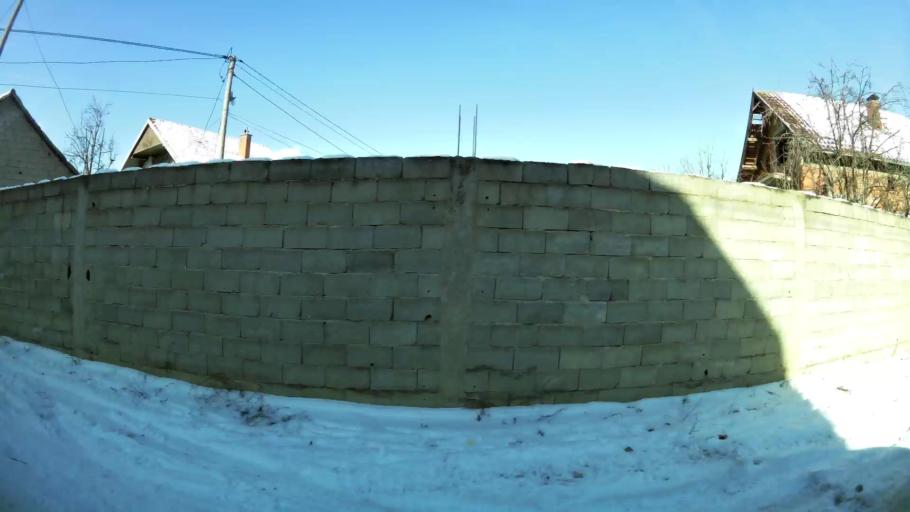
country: MK
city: Grchec
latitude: 41.9873
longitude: 21.3302
